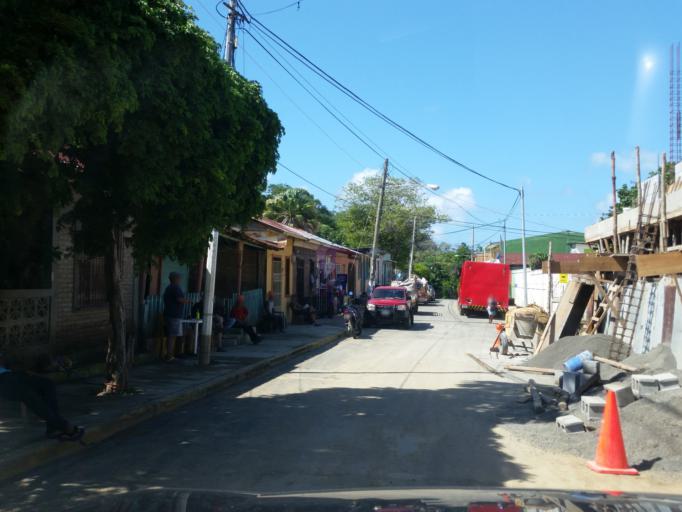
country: NI
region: Rivas
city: San Juan del Sur
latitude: 11.2520
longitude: -85.8707
